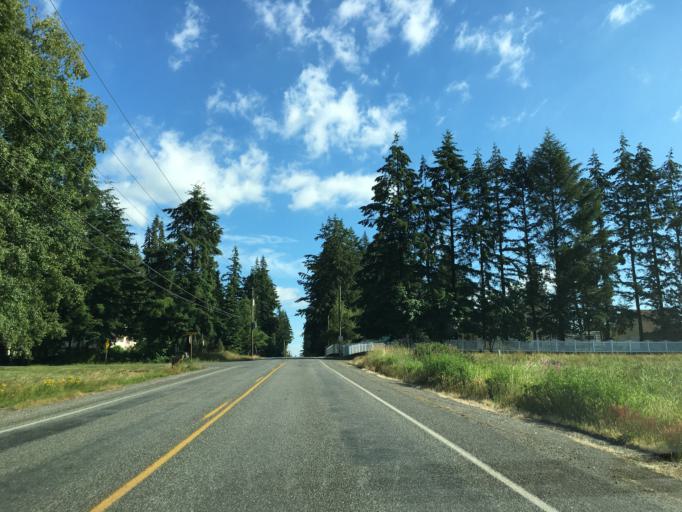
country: US
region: Washington
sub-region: Whatcom County
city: Ferndale
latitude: 48.9135
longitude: -122.5746
